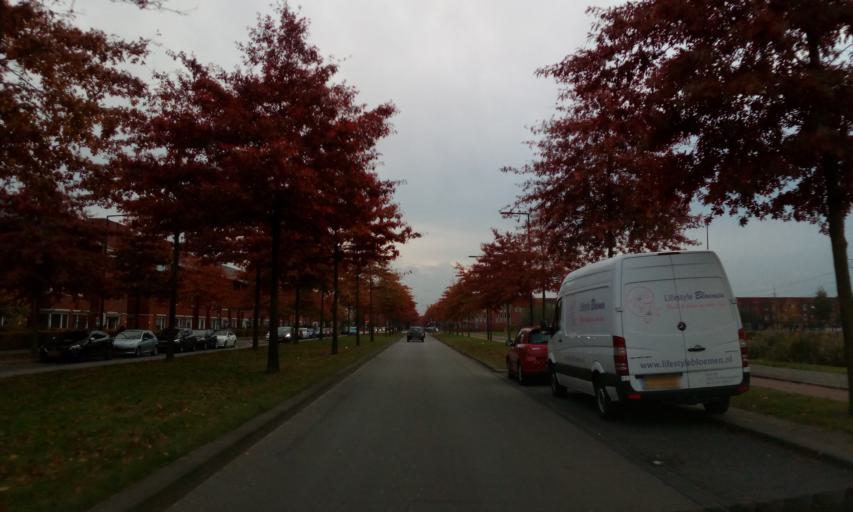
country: NL
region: South Holland
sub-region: Gemeente Capelle aan den IJssel
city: Capelle aan den IJssel
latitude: 51.9768
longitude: 4.5896
